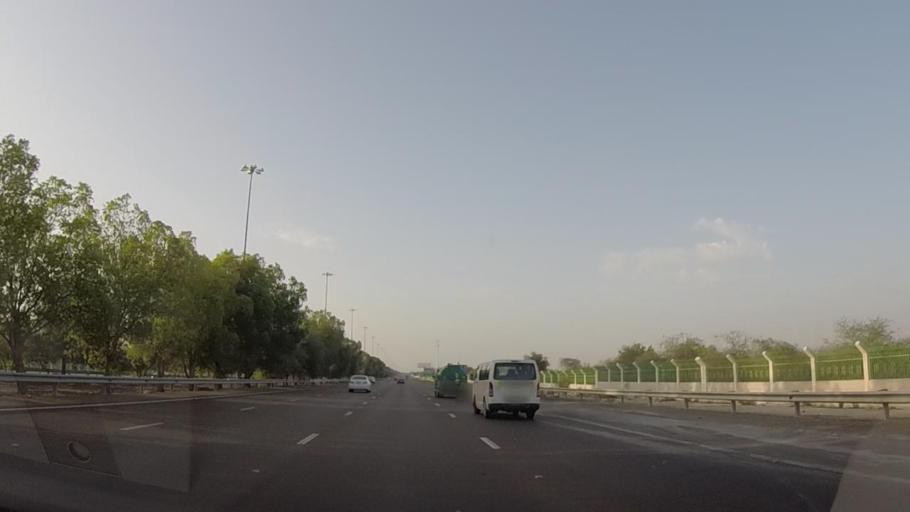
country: AE
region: Dubai
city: Dubai
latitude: 24.7879
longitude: 54.8578
